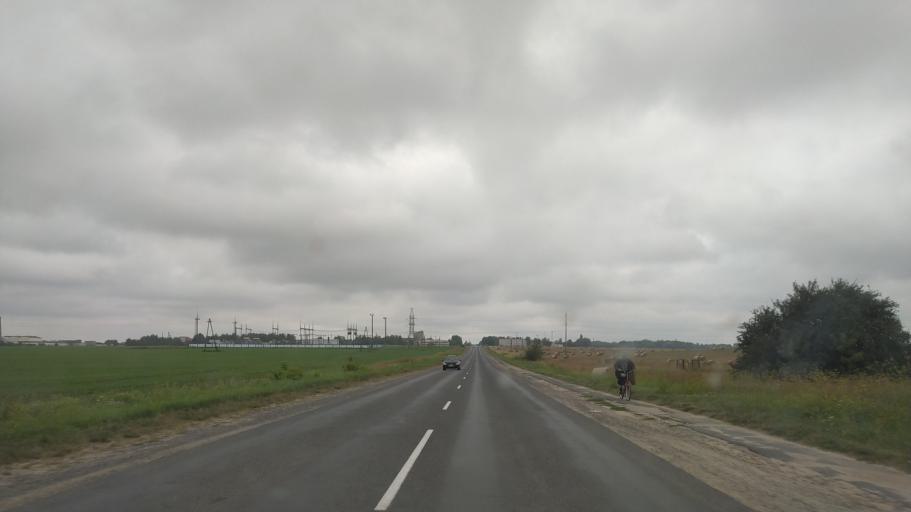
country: BY
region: Brest
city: Byaroza
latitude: 52.5466
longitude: 24.9552
